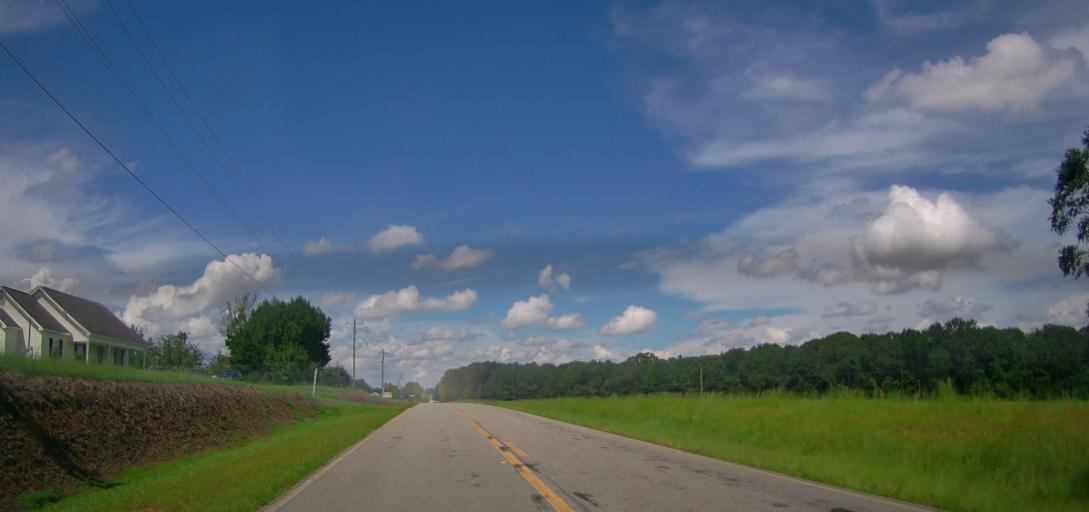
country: US
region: Georgia
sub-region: Peach County
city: Fort Valley
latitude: 32.4983
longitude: -83.8647
